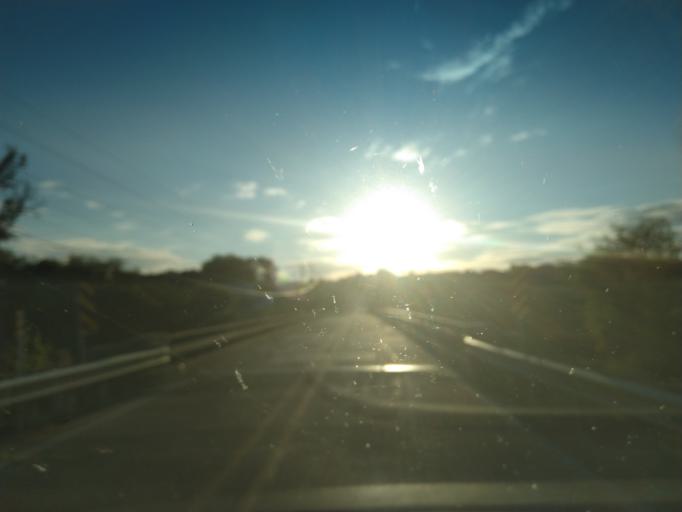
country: US
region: Iowa
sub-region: Jackson County
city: Maquoketa
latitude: 42.1645
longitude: -90.7282
